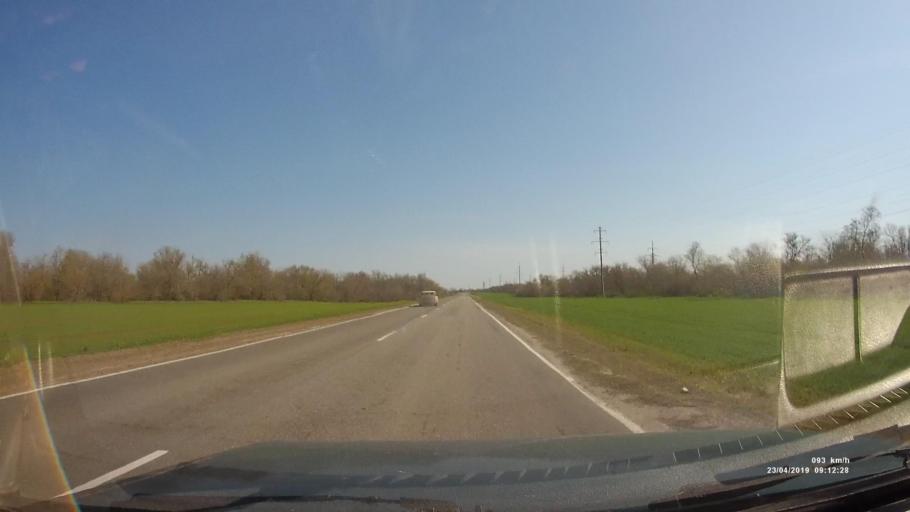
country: RU
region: Rostov
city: Proletarsk
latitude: 46.6073
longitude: 41.6409
